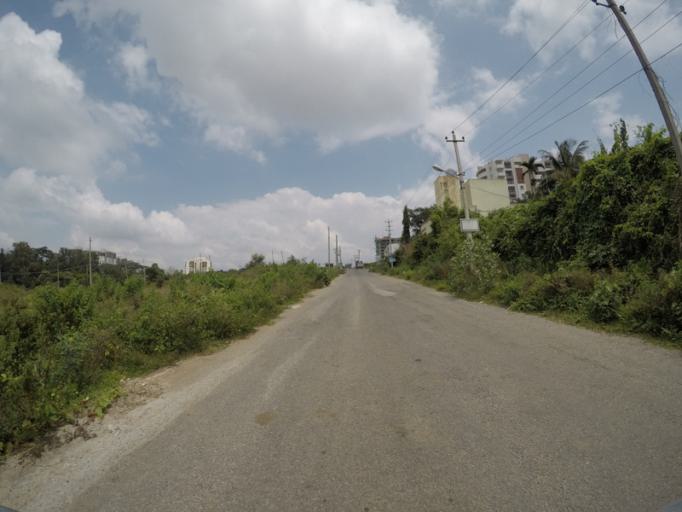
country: IN
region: Karnataka
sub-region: Bangalore Urban
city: Bangalore
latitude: 12.8622
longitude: 77.5261
